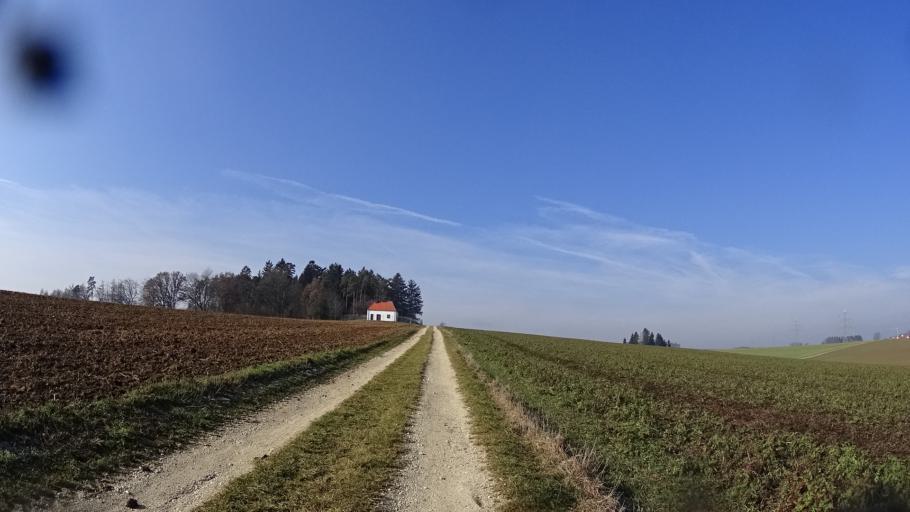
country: DE
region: Bavaria
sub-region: Upper Bavaria
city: Wettstetten
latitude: 48.8367
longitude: 11.3998
